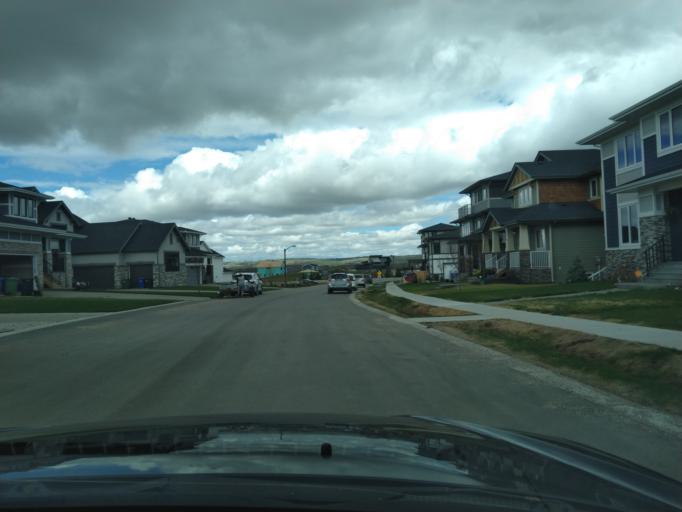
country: CA
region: Alberta
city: Cochrane
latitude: 51.1100
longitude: -114.3957
